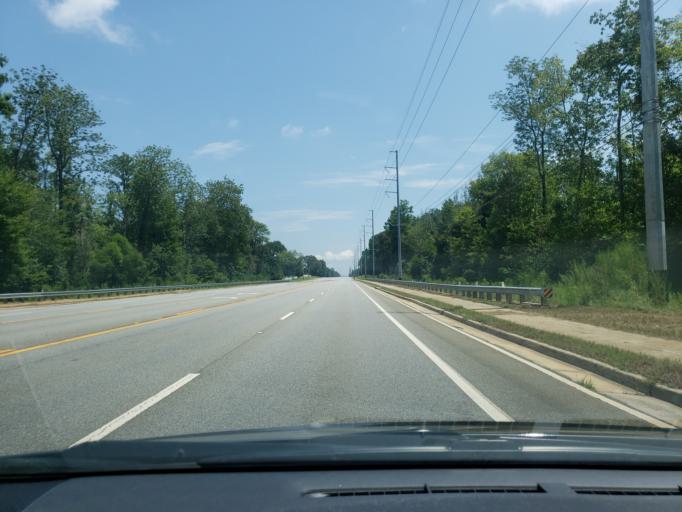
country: US
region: Georgia
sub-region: Dougherty County
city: Albany
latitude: 31.5856
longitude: -84.2658
